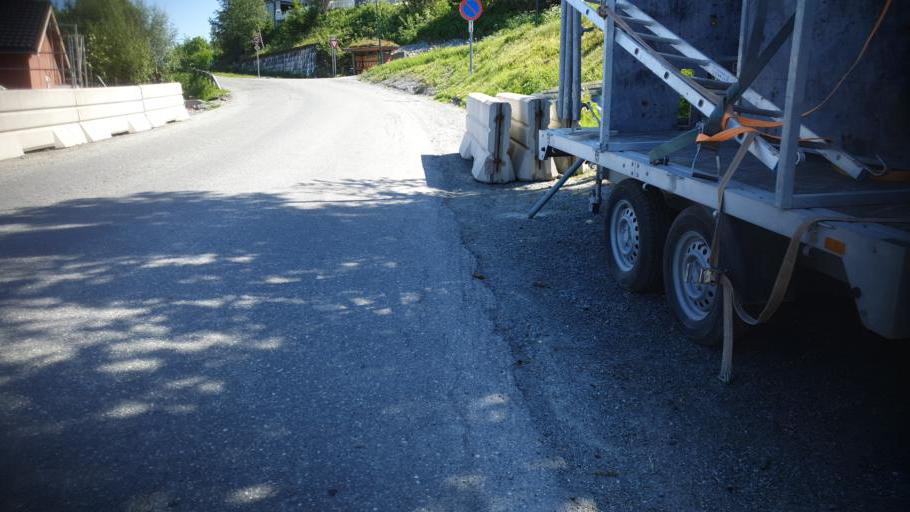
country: NO
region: Sor-Trondelag
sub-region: Malvik
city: Malvik
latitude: 63.4318
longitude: 10.6032
